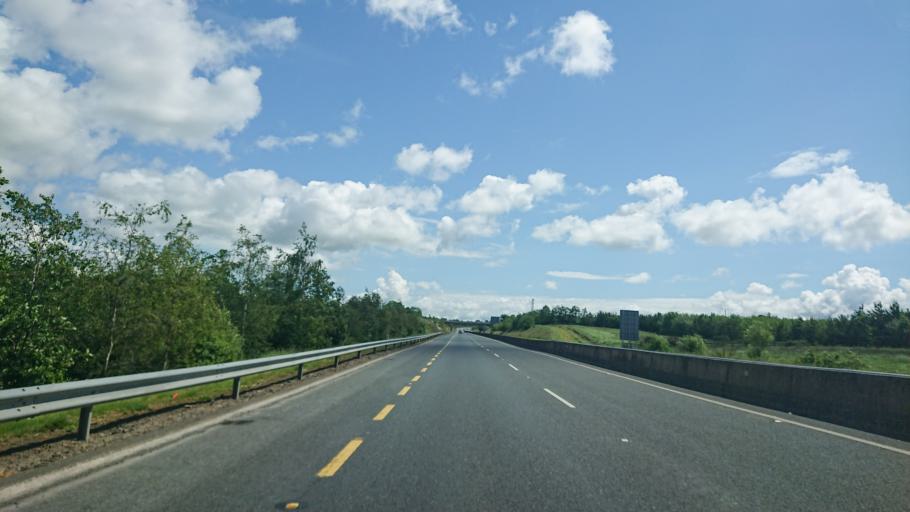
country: IE
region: Munster
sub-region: Waterford
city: Waterford
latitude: 52.2875
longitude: -7.1316
